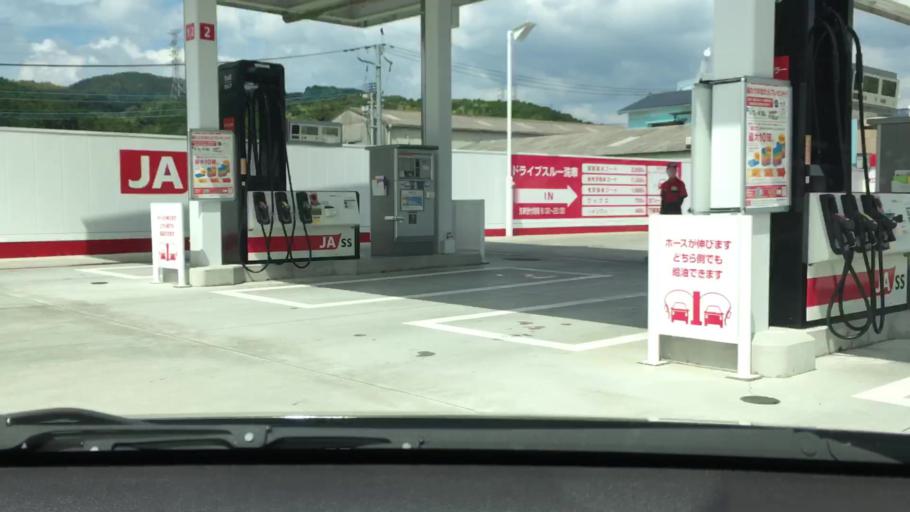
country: JP
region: Nagasaki
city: Sasebo
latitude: 33.2055
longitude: 129.6805
